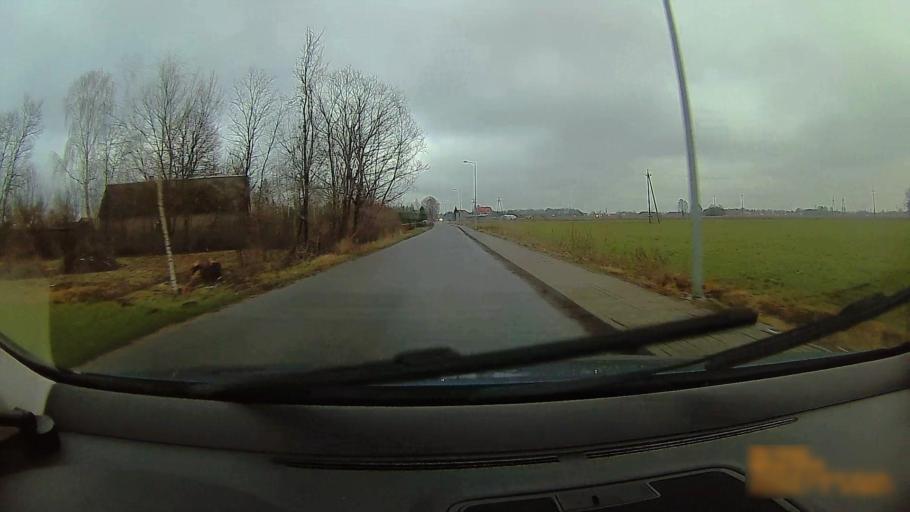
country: PL
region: Greater Poland Voivodeship
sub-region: Powiat koninski
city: Rychwal
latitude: 52.0758
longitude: 18.1480
